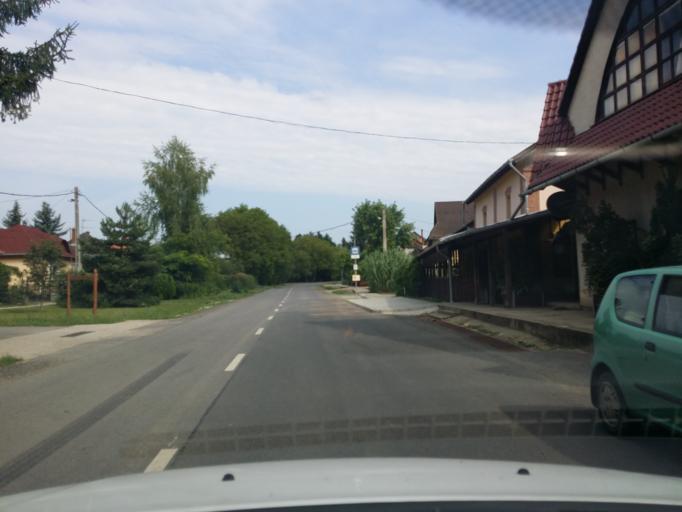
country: HU
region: Pest
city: Acsa
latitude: 47.7799
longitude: 19.3638
